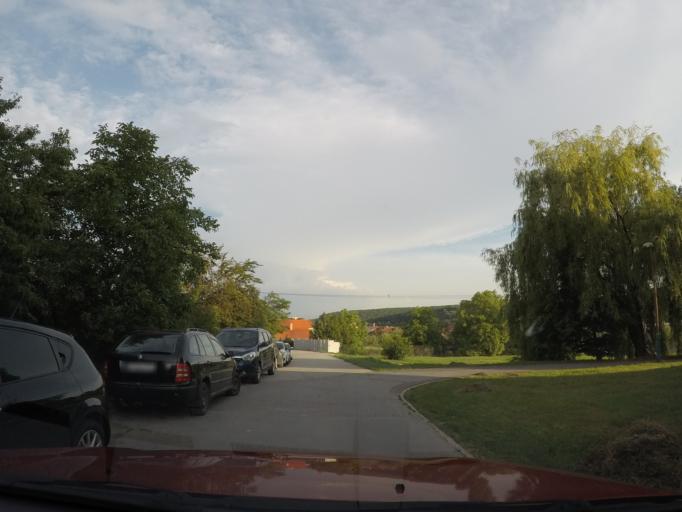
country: SK
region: Kosicky
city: Kosice
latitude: 48.7068
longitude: 21.2161
